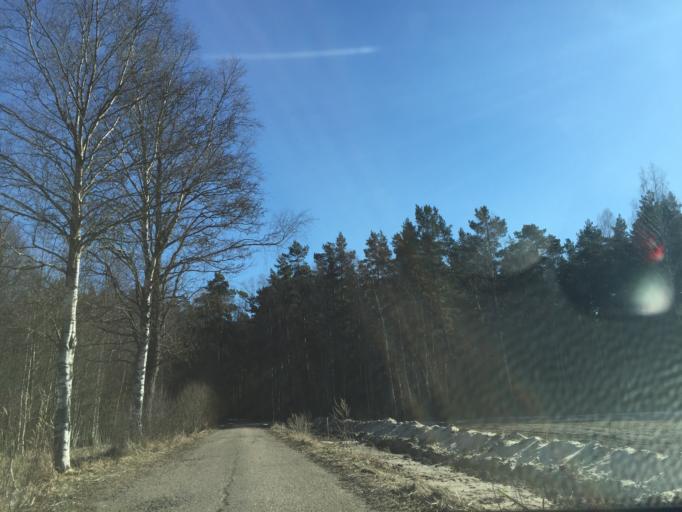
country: LV
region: Babite
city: Pinki
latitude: 56.9697
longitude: 23.9852
